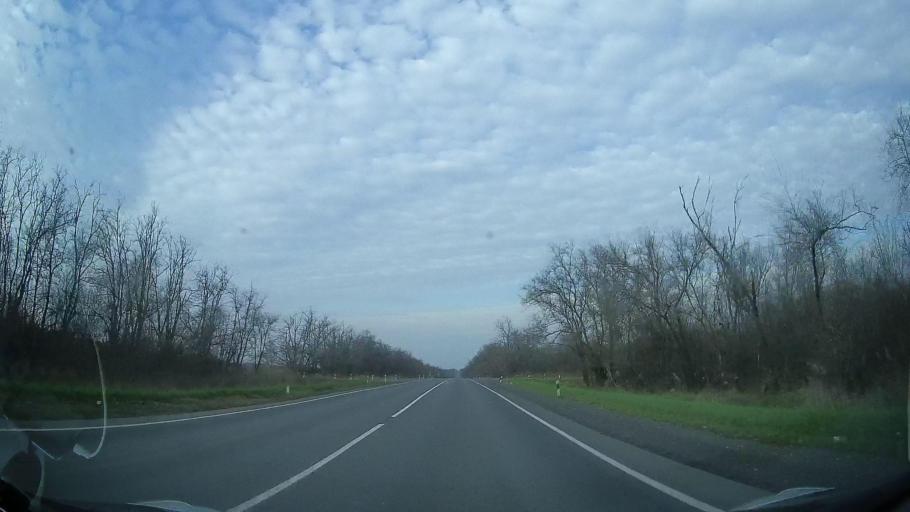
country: RU
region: Rostov
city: Bagayevskaya
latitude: 47.1032
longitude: 40.2767
